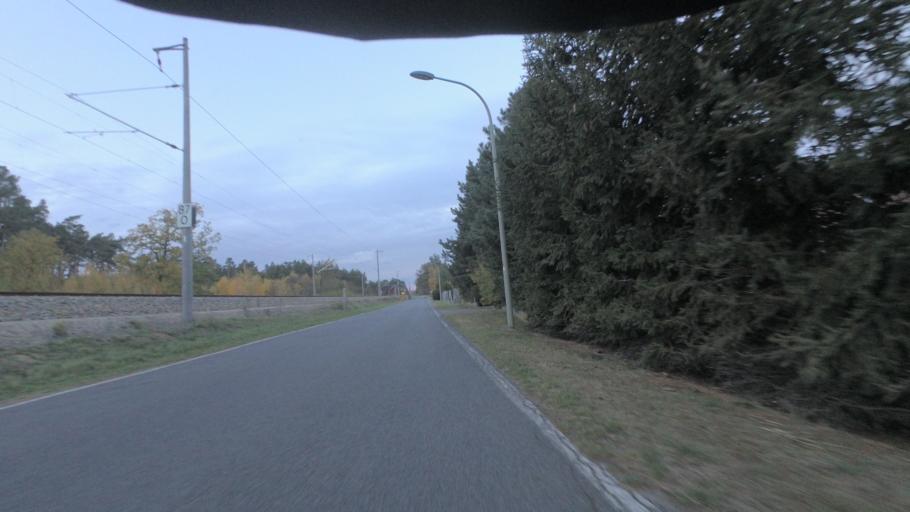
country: DE
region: Brandenburg
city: Sonnewalde
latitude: 51.7596
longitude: 13.6132
